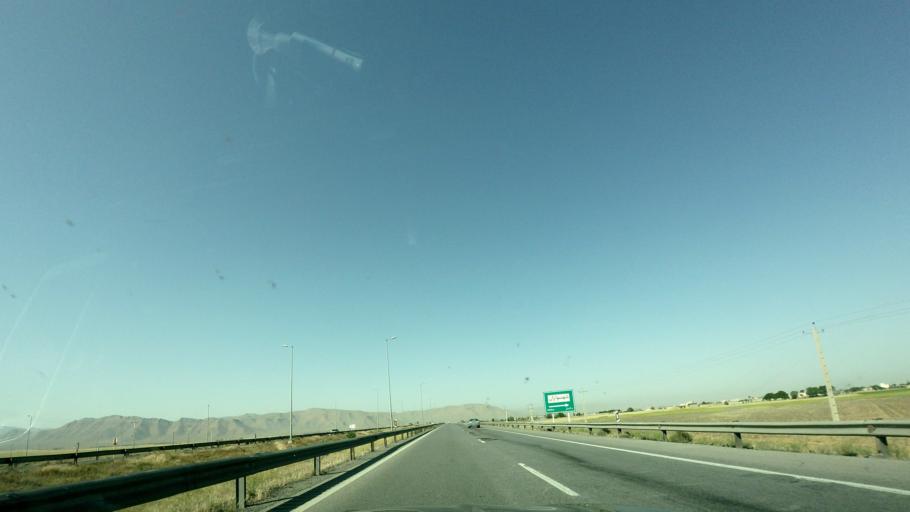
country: IR
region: Markazi
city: Ashtian
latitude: 34.1722
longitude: 50.0362
